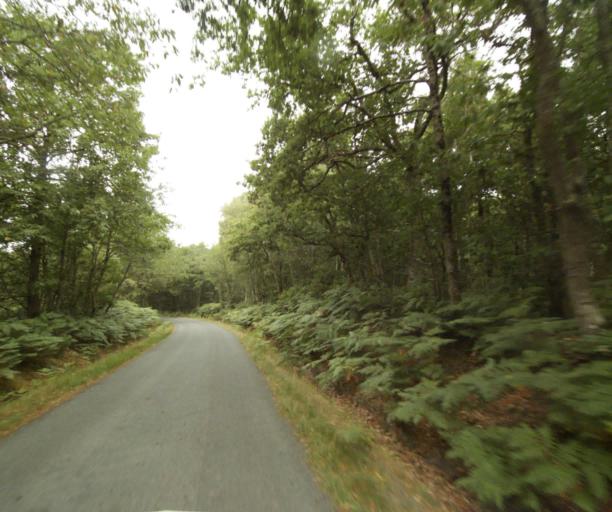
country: FR
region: Pays de la Loire
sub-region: Departement de la Sarthe
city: Sable-sur-Sarthe
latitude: 47.8118
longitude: -0.3704
